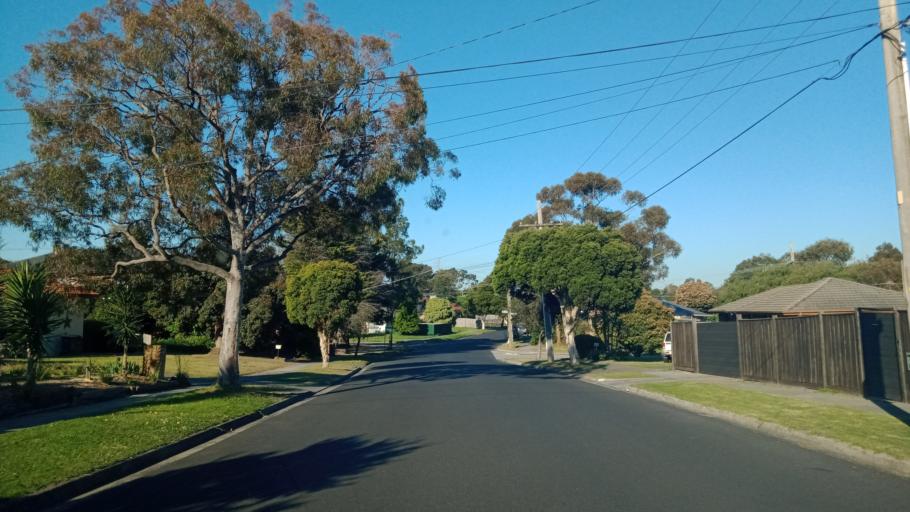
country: AU
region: Victoria
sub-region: Greater Dandenong
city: Noble Park North
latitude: -37.9310
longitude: 145.1771
